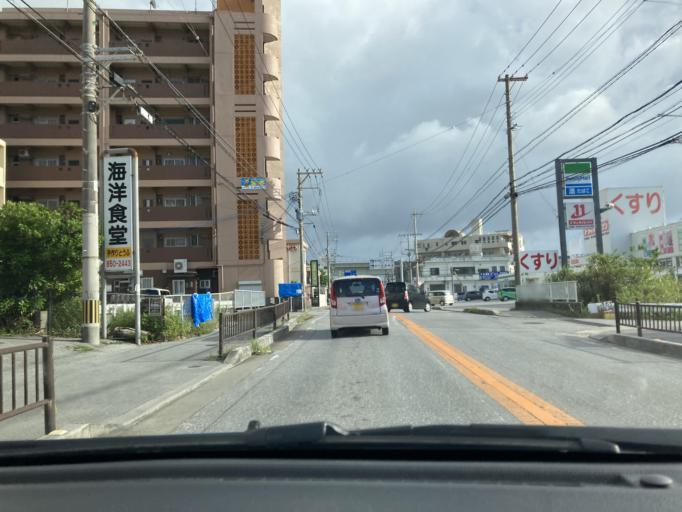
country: JP
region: Okinawa
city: Tomigusuku
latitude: 26.1768
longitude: 127.6655
